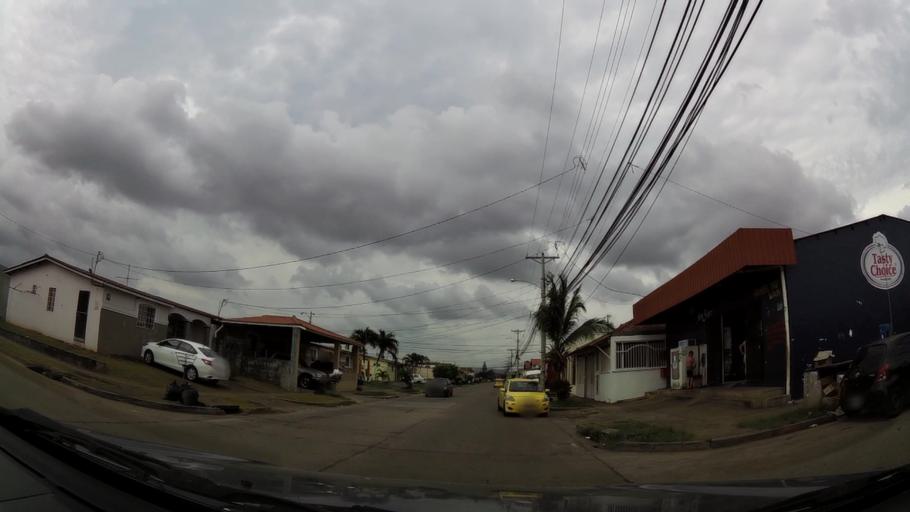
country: PA
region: Panama
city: Tocumen
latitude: 9.0431
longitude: -79.4096
